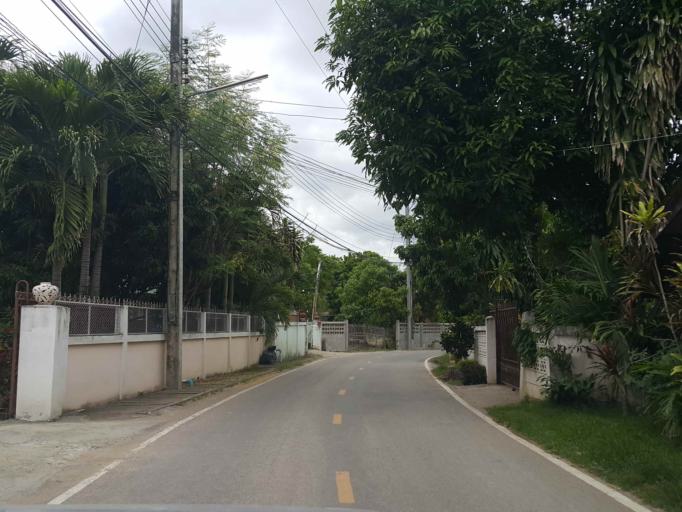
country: TH
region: Lamphun
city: Pa Sang
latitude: 18.4658
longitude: 98.9132
